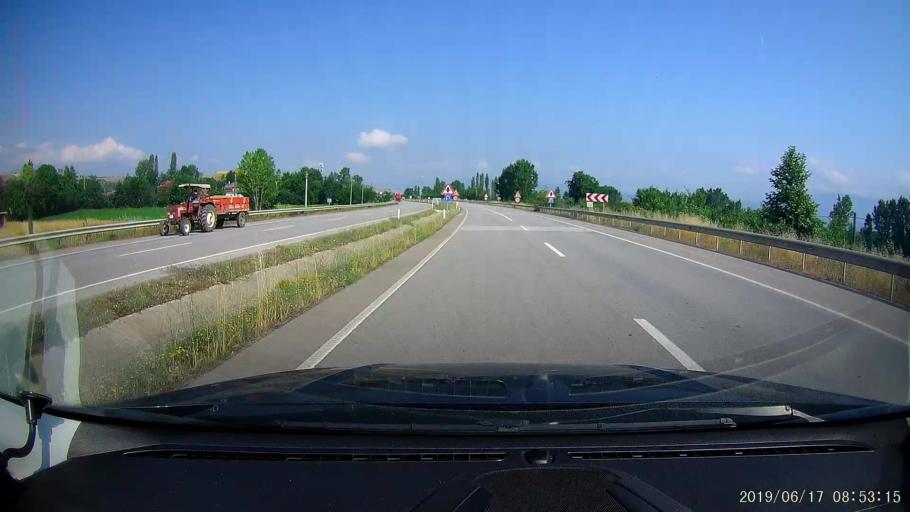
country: TR
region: Tokat
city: Erbaa
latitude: 40.7080
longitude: 36.4843
